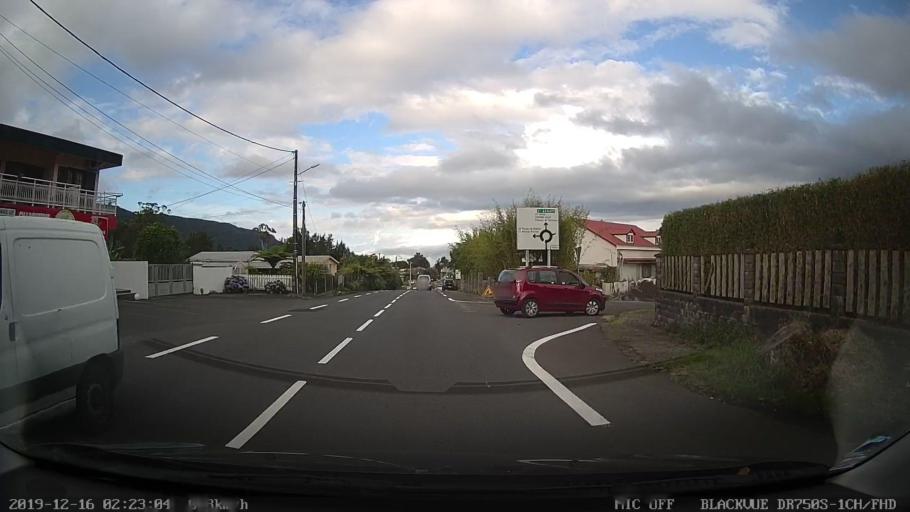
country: RE
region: Reunion
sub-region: Reunion
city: Salazie
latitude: -21.1446
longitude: 55.6193
